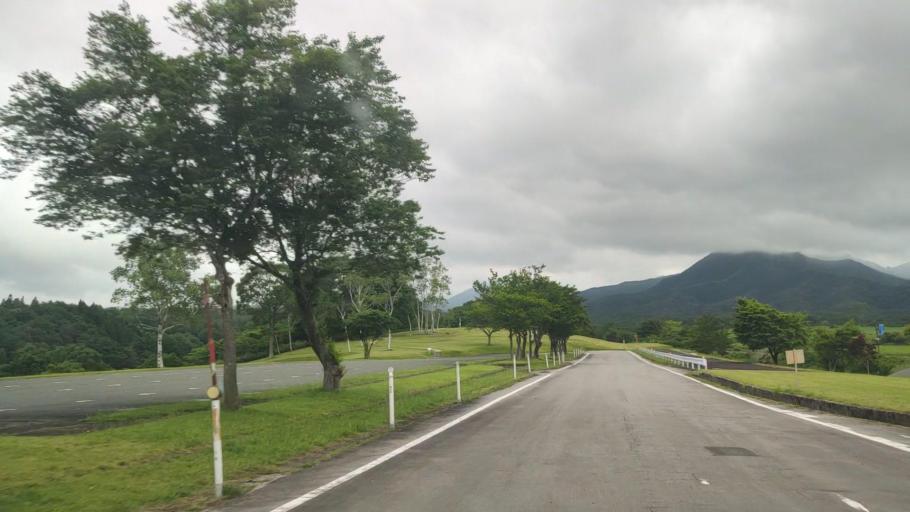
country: JP
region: Tottori
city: Kurayoshi
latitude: 35.2968
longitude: 133.6292
